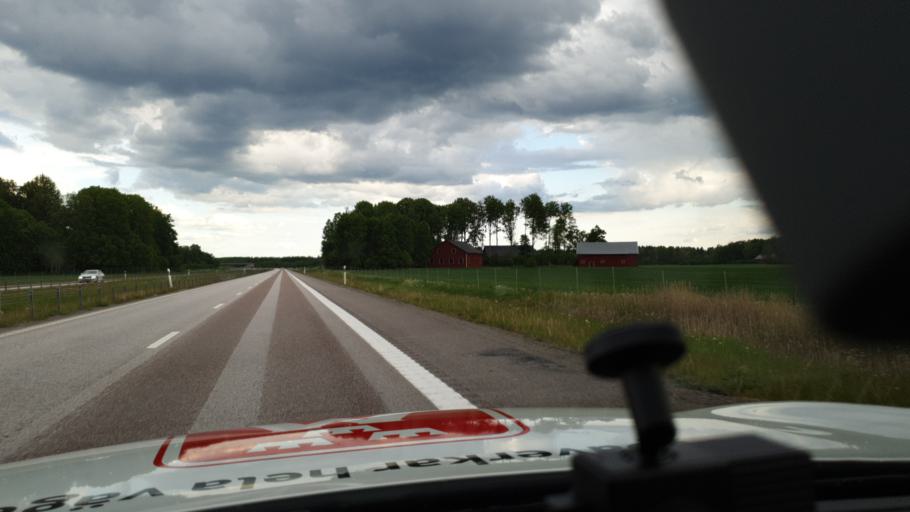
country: SE
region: Uppsala
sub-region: Osthammars Kommun
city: Bjorklinge
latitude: 60.0641
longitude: 17.6103
